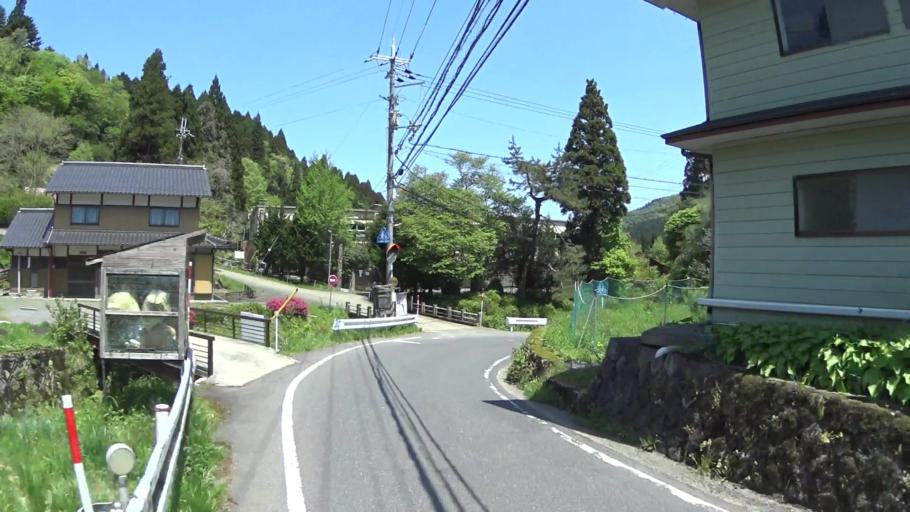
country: JP
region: Shiga Prefecture
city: Kitahama
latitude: 35.1683
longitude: 135.7845
